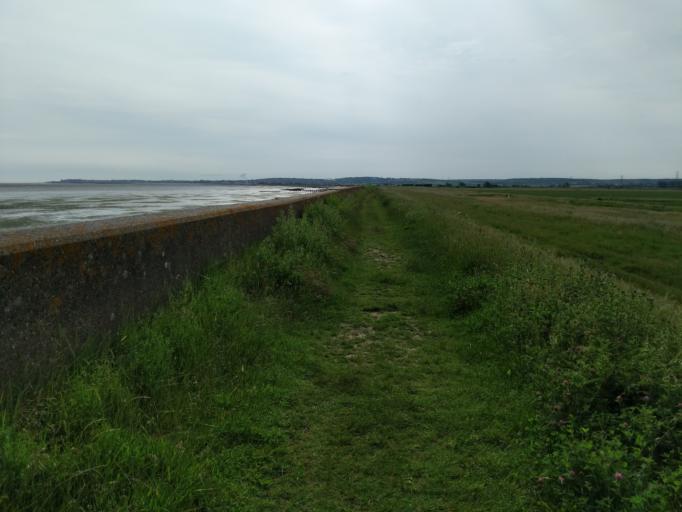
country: GB
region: England
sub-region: Kent
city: Leysdown-on-Sea
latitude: 51.3462
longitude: 0.9434
